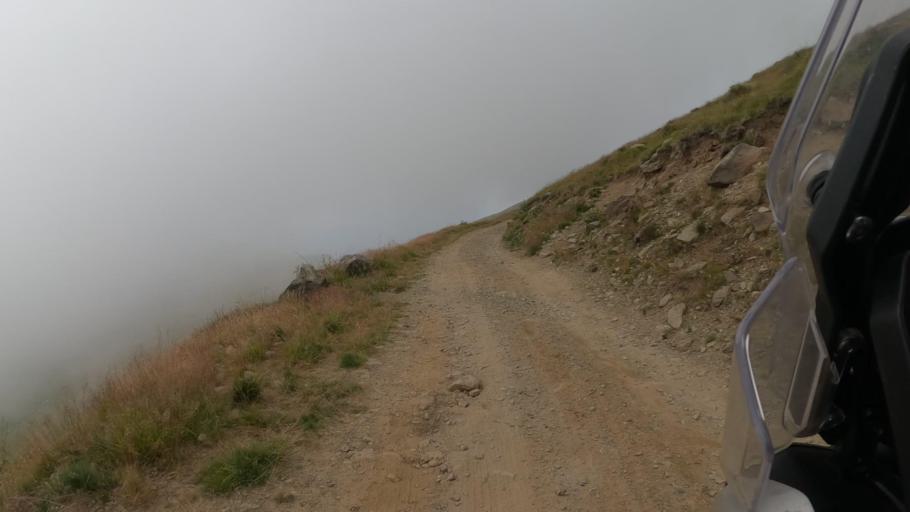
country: IT
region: Piedmont
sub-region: Provincia di Torino
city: Lemie
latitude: 45.1754
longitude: 7.2823
